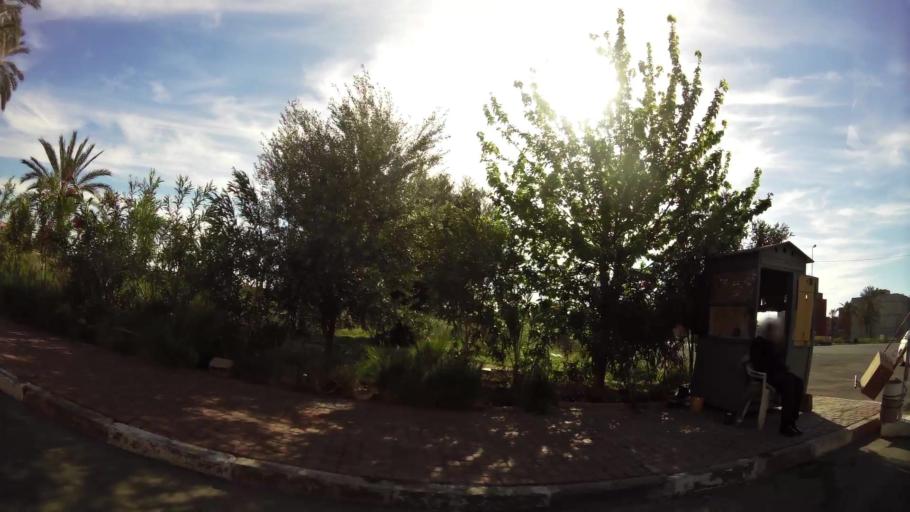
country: MA
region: Marrakech-Tensift-Al Haouz
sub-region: Marrakech
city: Marrakesh
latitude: 31.6778
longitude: -8.0556
